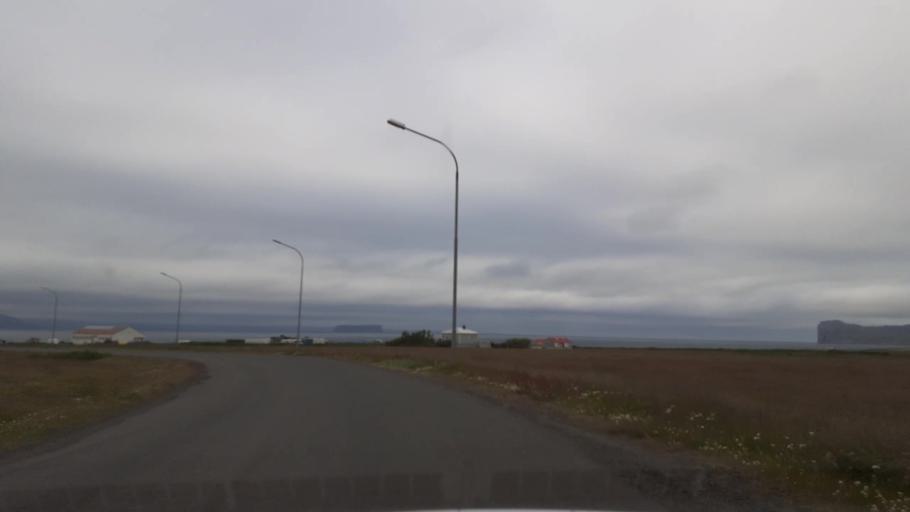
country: IS
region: Northwest
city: Saudarkrokur
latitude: 65.9008
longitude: -19.4172
